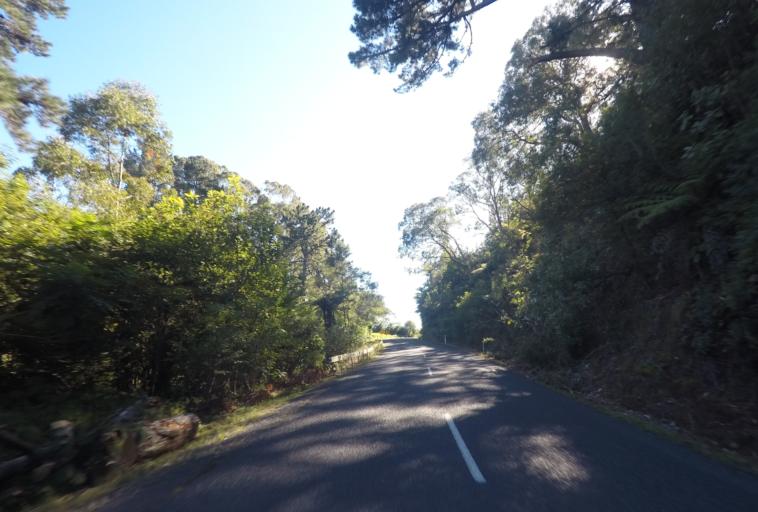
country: NZ
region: Bay of Plenty
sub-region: Western Bay of Plenty District
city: Waihi Beach
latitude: -37.3928
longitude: 175.9045
